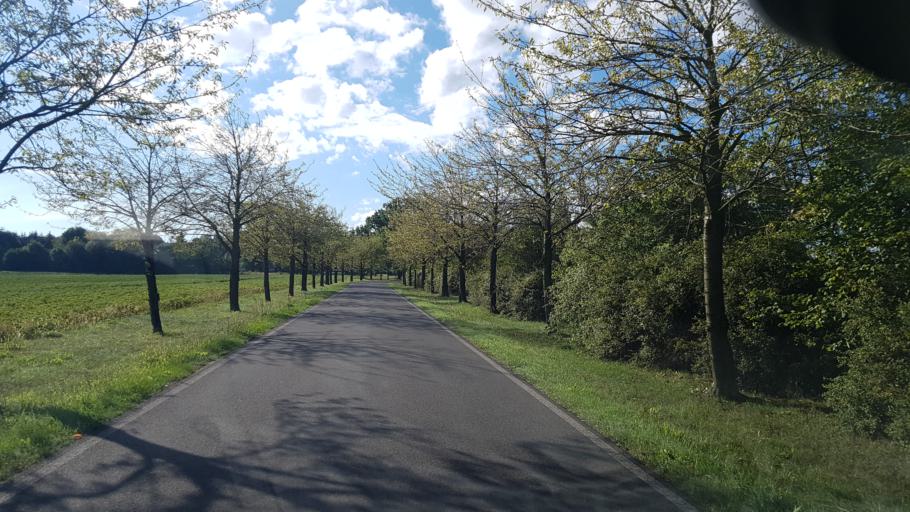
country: DE
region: Saxony
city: Gross Duben
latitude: 51.6259
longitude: 14.5338
